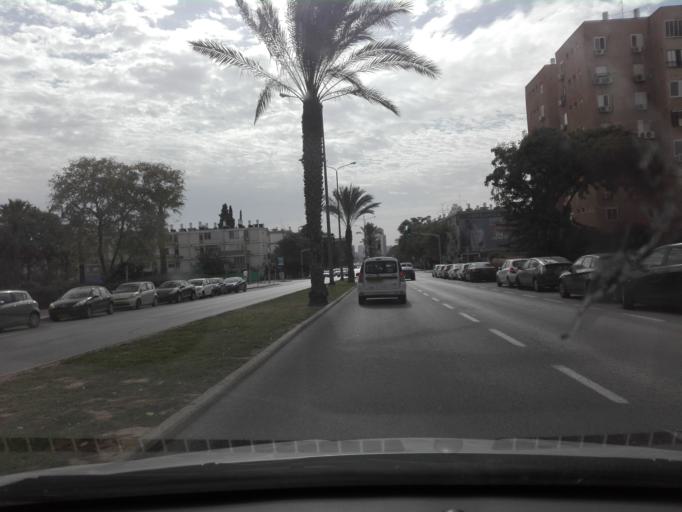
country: IL
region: Southern District
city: Beersheba
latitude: 31.2670
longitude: 34.7981
